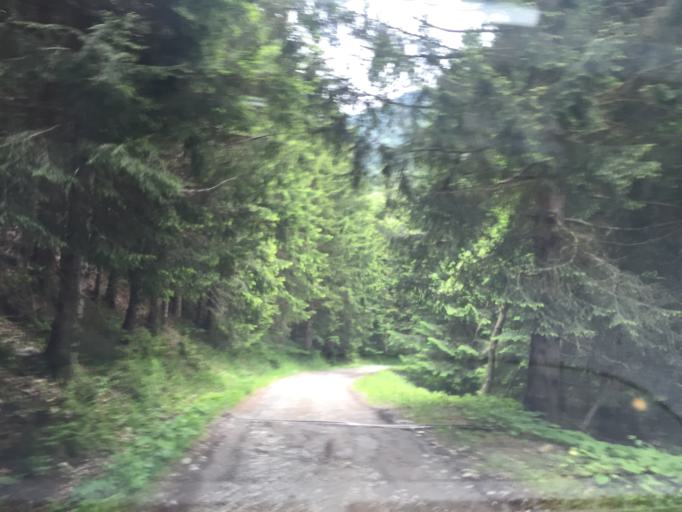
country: FR
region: Rhone-Alpes
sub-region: Departement de la Savoie
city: La Rochette
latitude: 45.4346
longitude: 6.1752
